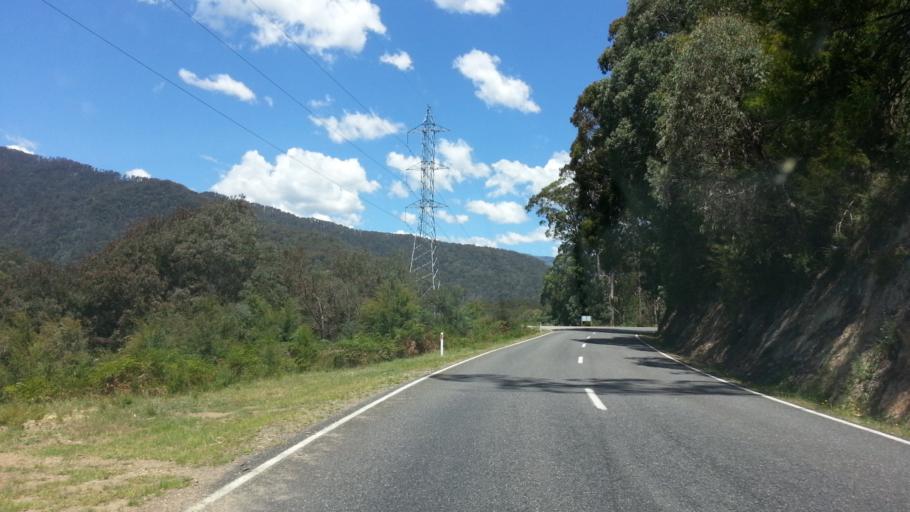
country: AU
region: Victoria
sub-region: Alpine
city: Mount Beauty
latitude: -36.7686
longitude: 147.2136
